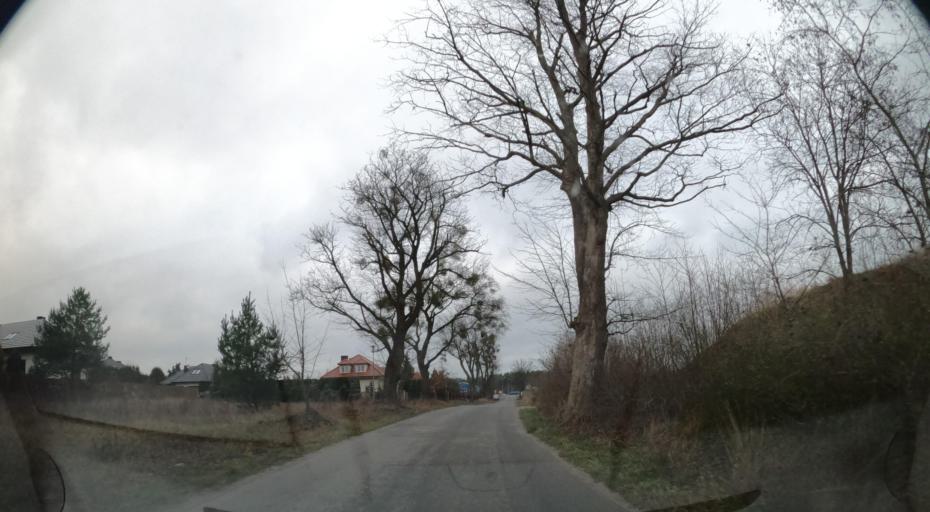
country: PL
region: Kujawsko-Pomorskie
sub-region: Powiat bydgoski
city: Sicienko
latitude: 53.1560
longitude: 17.8484
